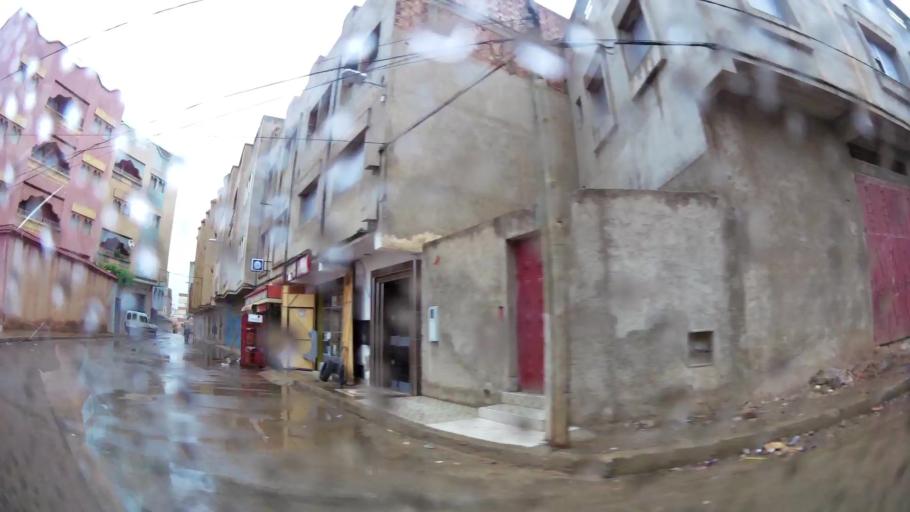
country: MA
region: Oriental
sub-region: Nador
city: Boudinar
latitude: 35.1153
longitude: -3.6438
